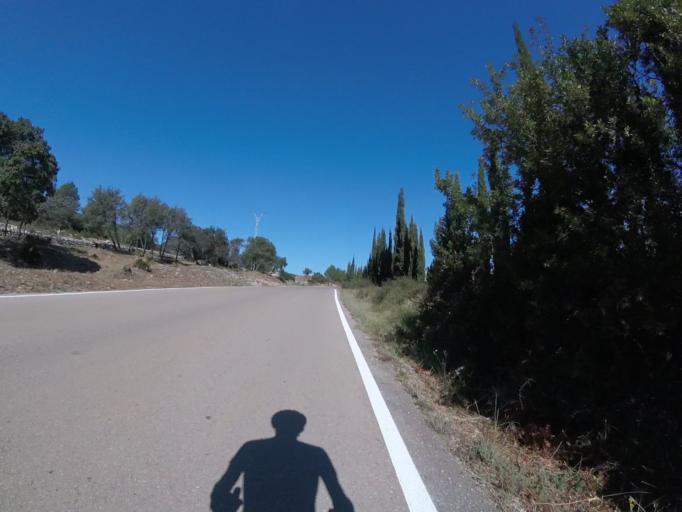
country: ES
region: Valencia
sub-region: Provincia de Castello
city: Santa Magdalena de Pulpis
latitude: 40.3665
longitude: 0.2762
